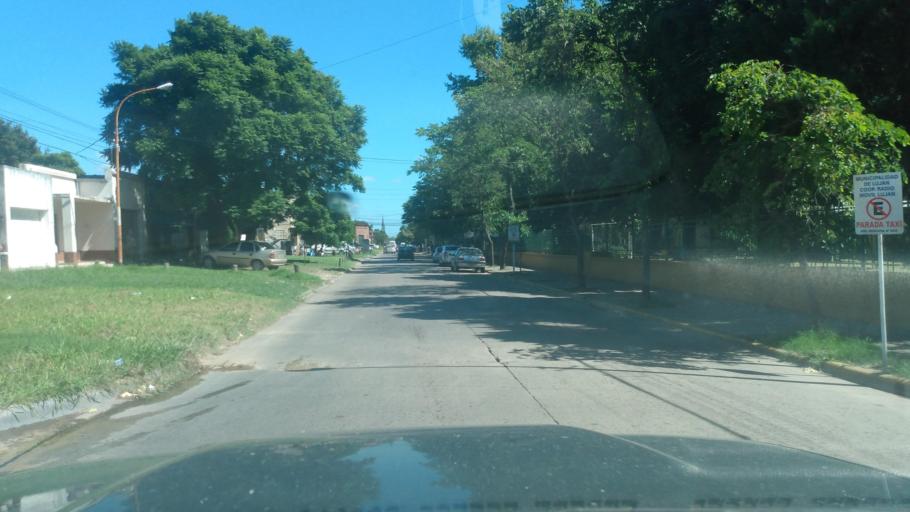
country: AR
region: Buenos Aires
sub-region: Partido de Lujan
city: Lujan
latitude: -34.5711
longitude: -59.0970
